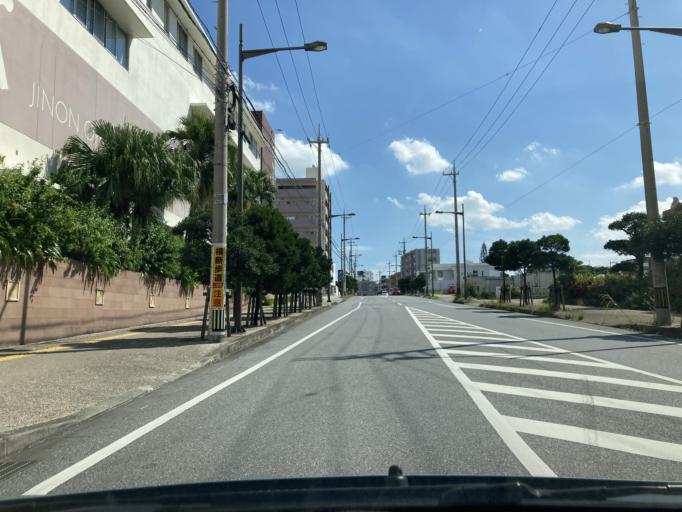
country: JP
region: Okinawa
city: Ginowan
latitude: 26.2725
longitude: 127.7305
